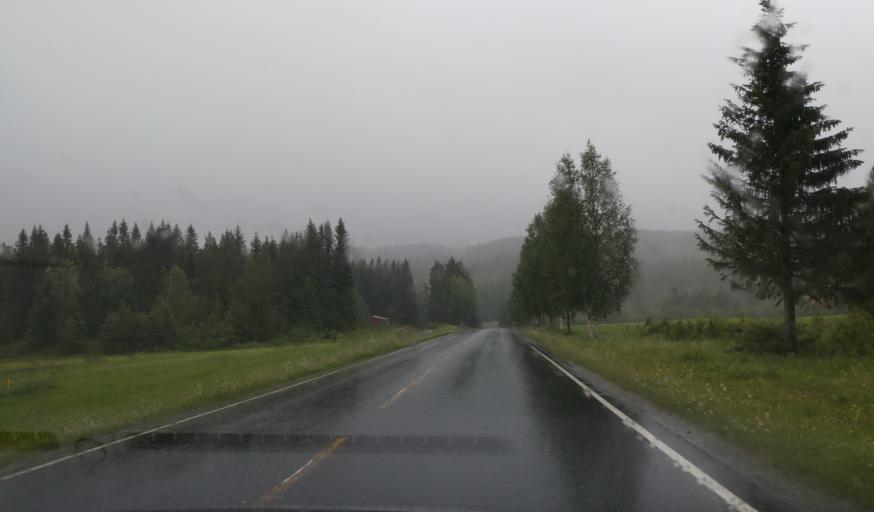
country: NO
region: Sor-Trondelag
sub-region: Selbu
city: Mebonden
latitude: 63.3740
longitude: 11.0760
